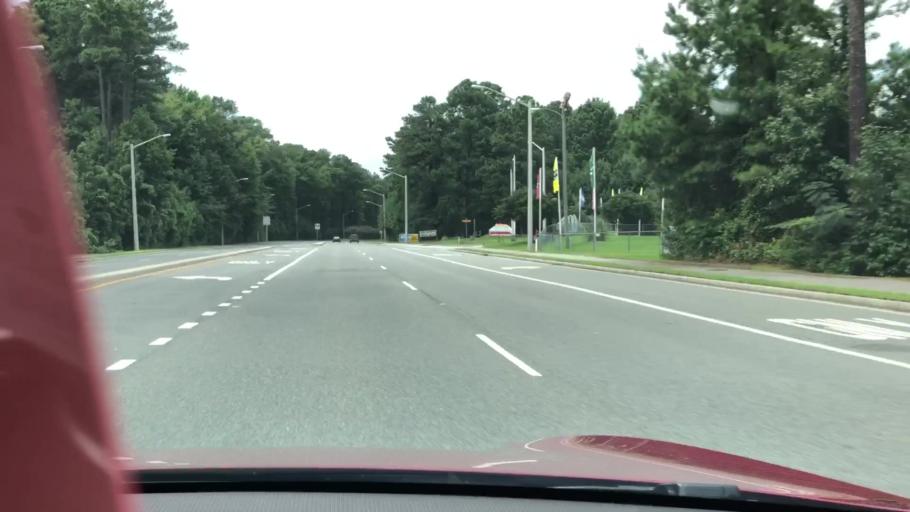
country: US
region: Virginia
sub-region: City of Virginia Beach
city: Virginia Beach
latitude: 36.8154
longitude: -75.9972
